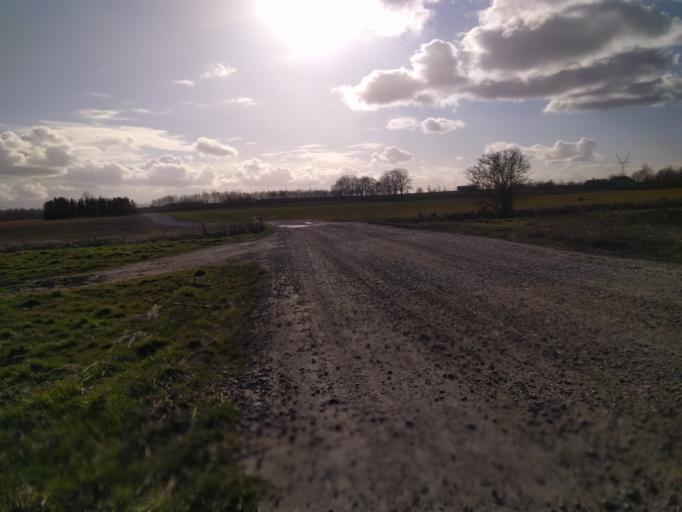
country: DK
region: South Denmark
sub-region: Kerteminde Kommune
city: Langeskov
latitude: 55.3677
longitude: 10.5222
